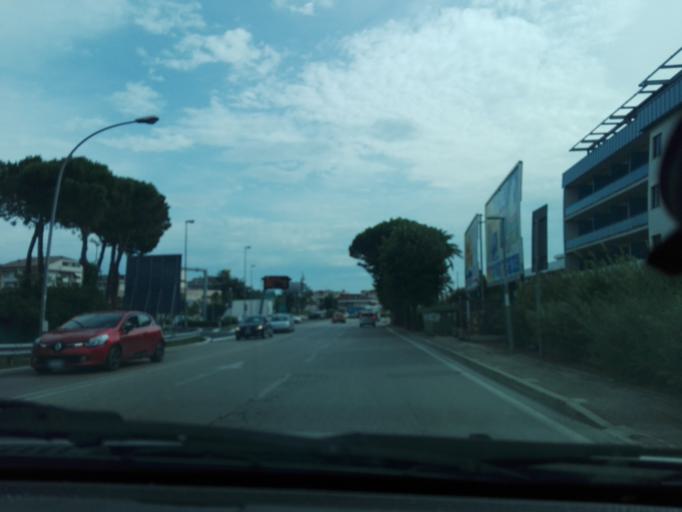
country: IT
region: Abruzzo
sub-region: Provincia di Pescara
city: San Martino Bassa
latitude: 42.5204
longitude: 14.1372
